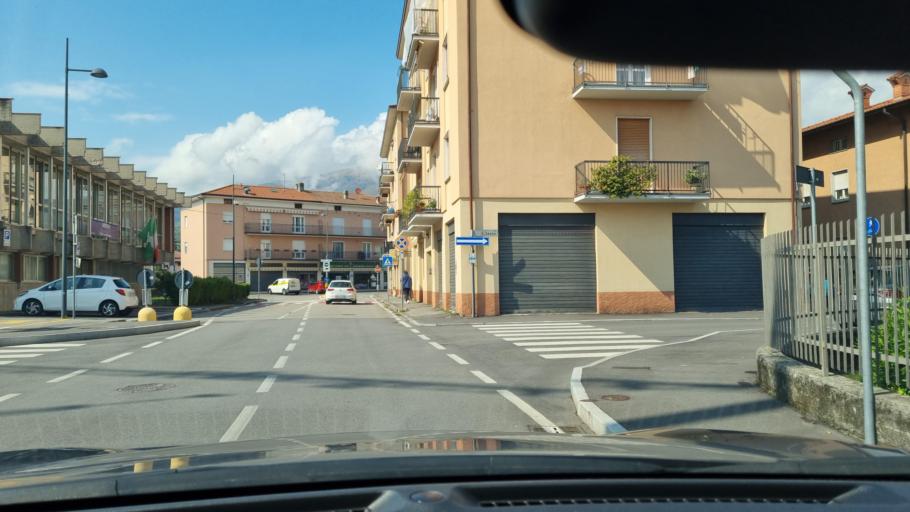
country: IT
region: Lombardy
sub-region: Provincia di Bergamo
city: Ambivere
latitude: 45.7197
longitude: 9.5493
